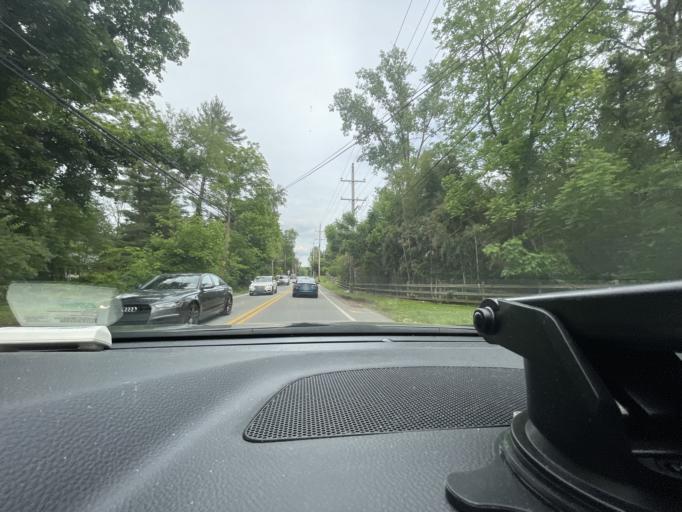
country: US
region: Pennsylvania
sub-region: Montgomery County
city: Blue Bell
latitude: 40.1655
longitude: -75.2622
